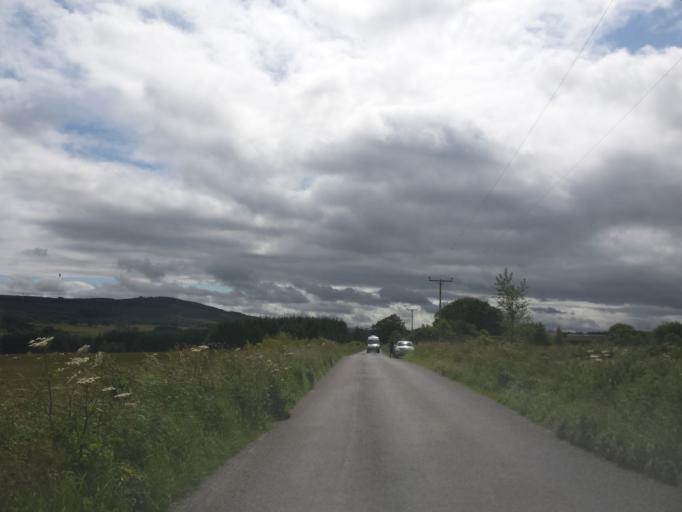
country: GB
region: Scotland
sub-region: Highland
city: Fortrose
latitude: 57.4751
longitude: -4.0874
